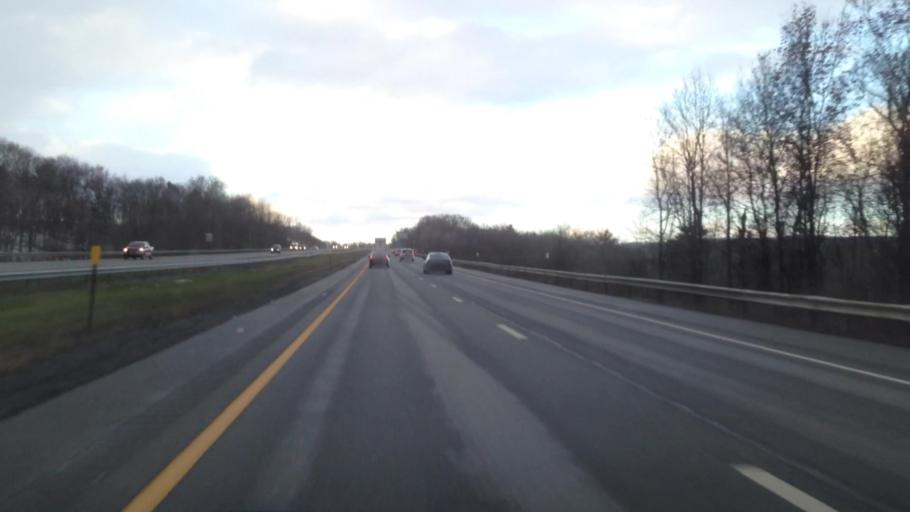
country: US
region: New York
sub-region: Herkimer County
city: Little Falls
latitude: 43.0107
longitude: -74.7906
